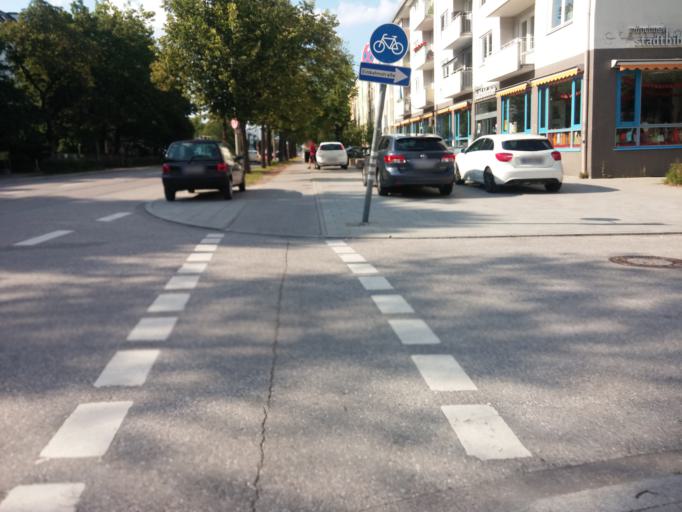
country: DE
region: Bavaria
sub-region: Upper Bavaria
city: Munich
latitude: 48.1826
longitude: 11.5669
